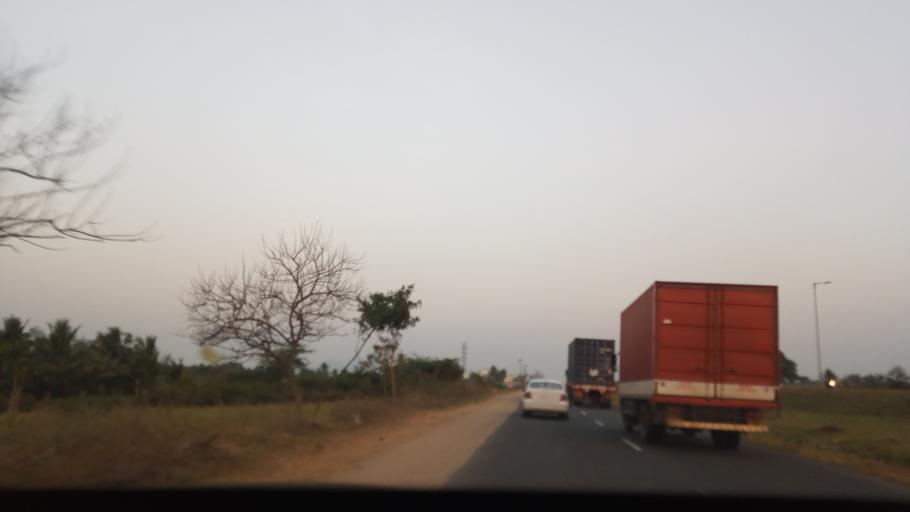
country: IN
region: Tamil Nadu
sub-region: Salem
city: Salem
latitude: 11.6642
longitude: 78.2395
